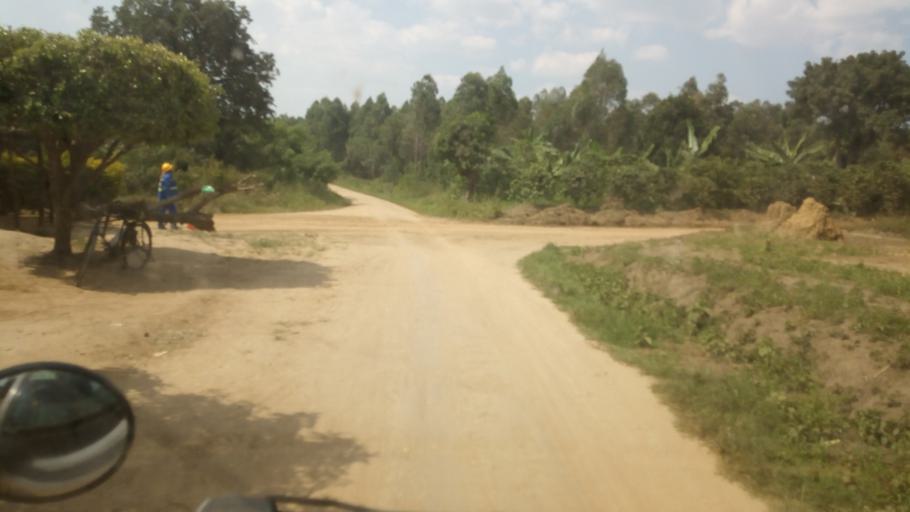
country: UG
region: Western Region
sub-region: Kanungu District
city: Ntungamo
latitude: -0.7825
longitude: 29.6913
